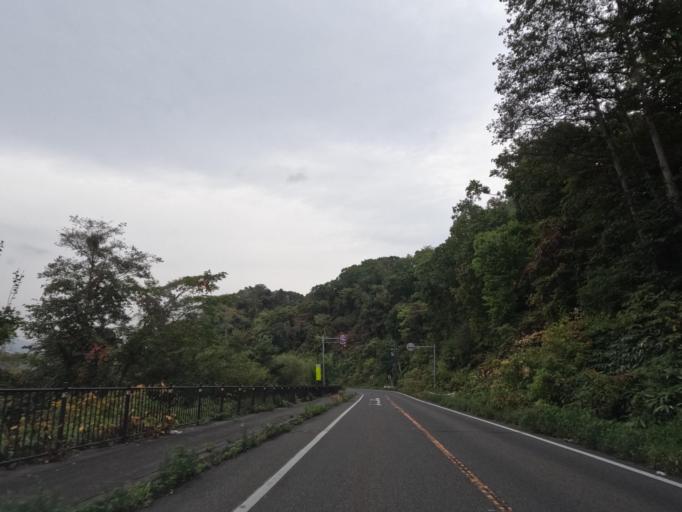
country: JP
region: Hokkaido
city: Date
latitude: 42.5319
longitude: 140.8604
